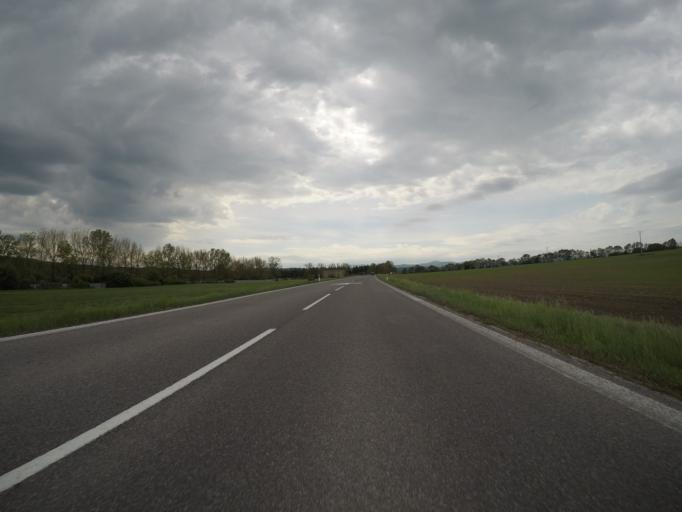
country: SK
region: Banskobystricky
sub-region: Okres Banska Bystrica
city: Banska Bystrica
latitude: 48.6643
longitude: 19.1409
